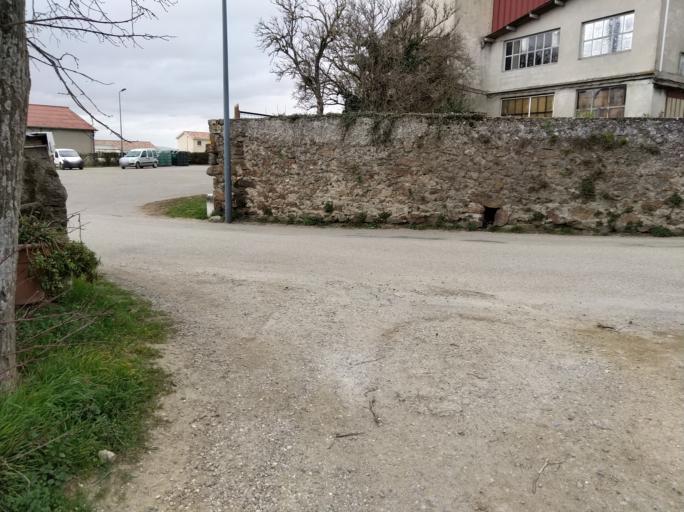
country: FR
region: Rhone-Alpes
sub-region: Departement de l'Ardeche
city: Felines
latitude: 45.3366
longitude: 4.7429
